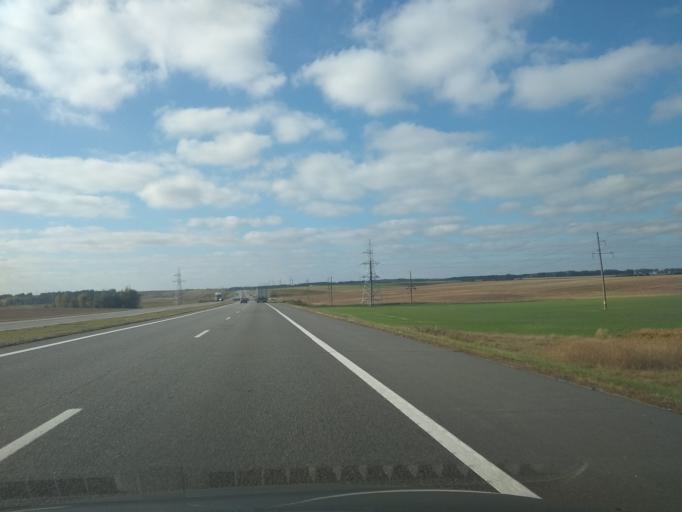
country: BY
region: Minsk
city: Stowbtsy
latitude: 53.5247
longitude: 26.7191
